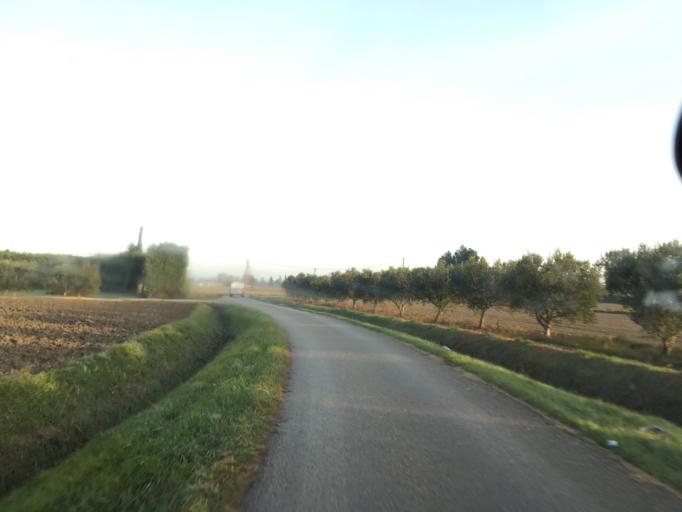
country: FR
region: Provence-Alpes-Cote d'Azur
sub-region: Departement du Vaucluse
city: Caderousse
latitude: 44.1168
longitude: 4.7636
